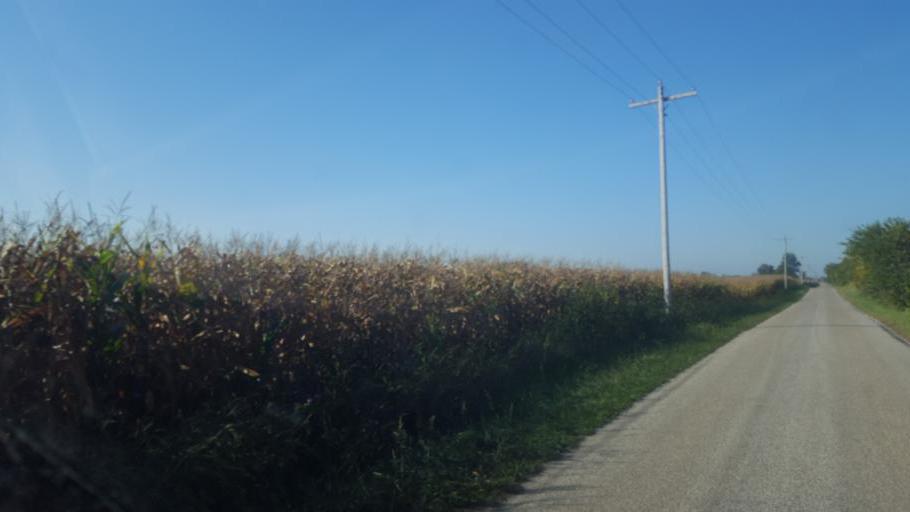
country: US
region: Ohio
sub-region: Union County
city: Richwood
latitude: 40.5363
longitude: -83.3654
